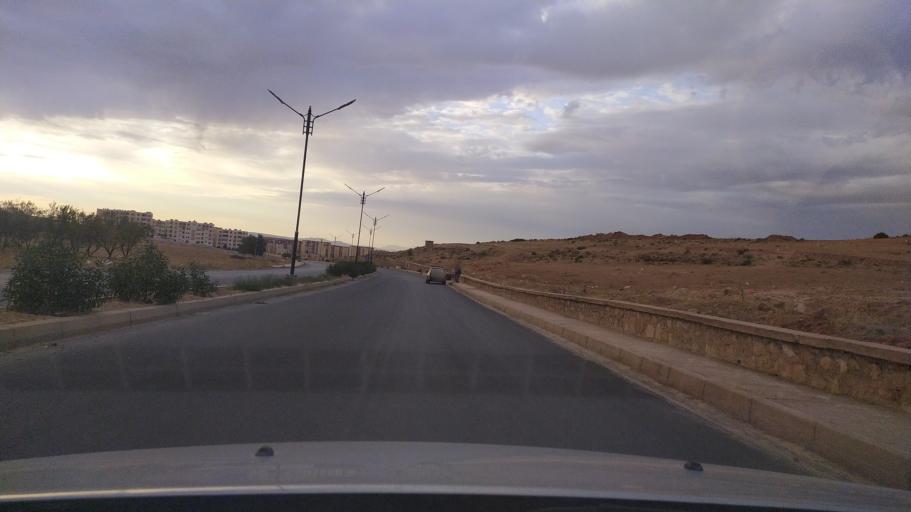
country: DZ
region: Tiaret
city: Frenda
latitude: 35.0519
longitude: 1.0675
